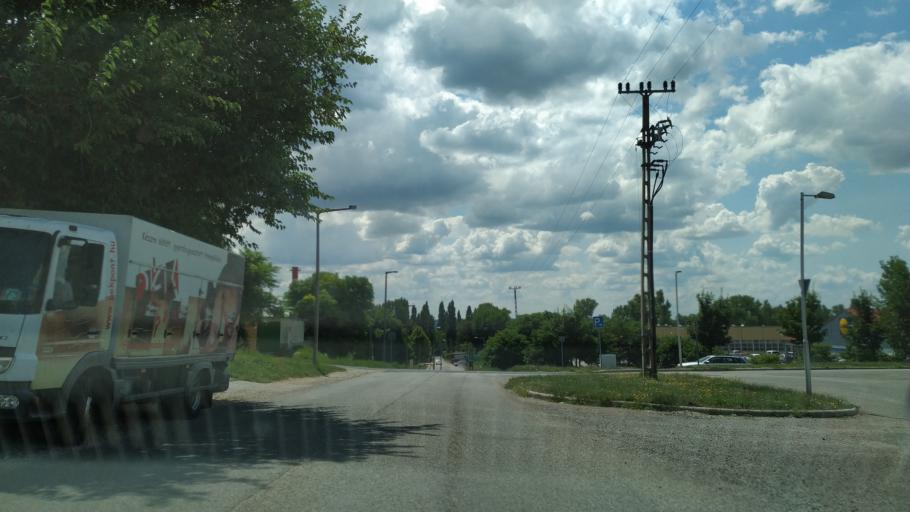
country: HU
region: Veszprem
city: Varpalota
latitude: 47.2017
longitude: 18.1474
